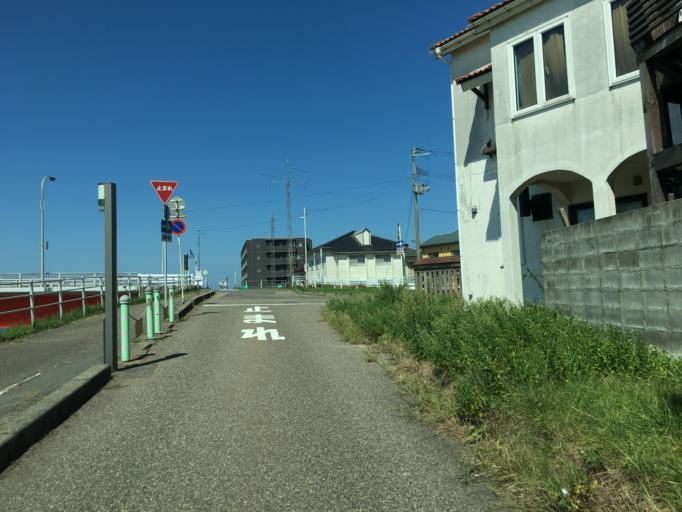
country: JP
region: Niigata
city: Niigata-shi
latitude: 37.9052
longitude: 139.0073
